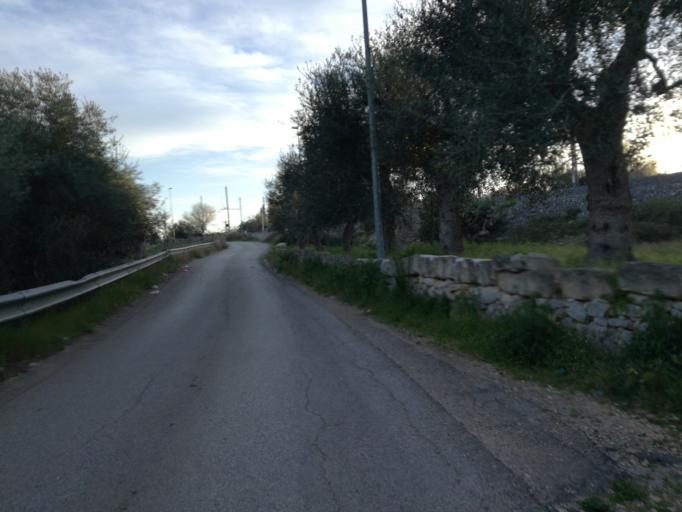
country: IT
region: Apulia
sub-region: Provincia di Bari
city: Lamie
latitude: 41.0346
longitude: 16.8798
